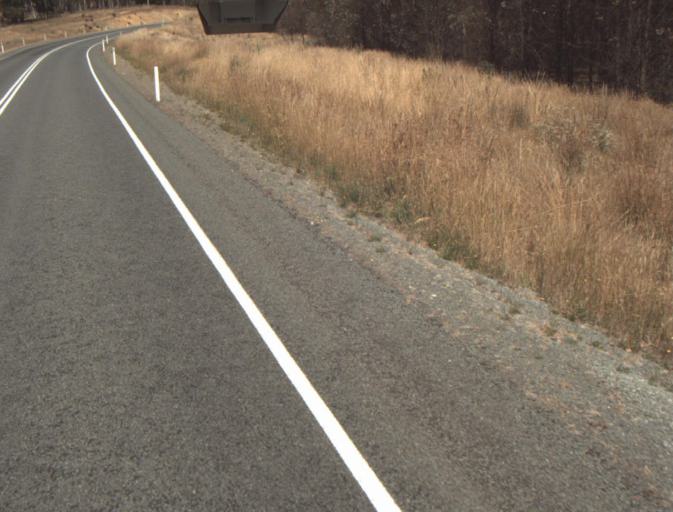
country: AU
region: Tasmania
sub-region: Launceston
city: Newstead
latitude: -41.3378
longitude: 147.3474
